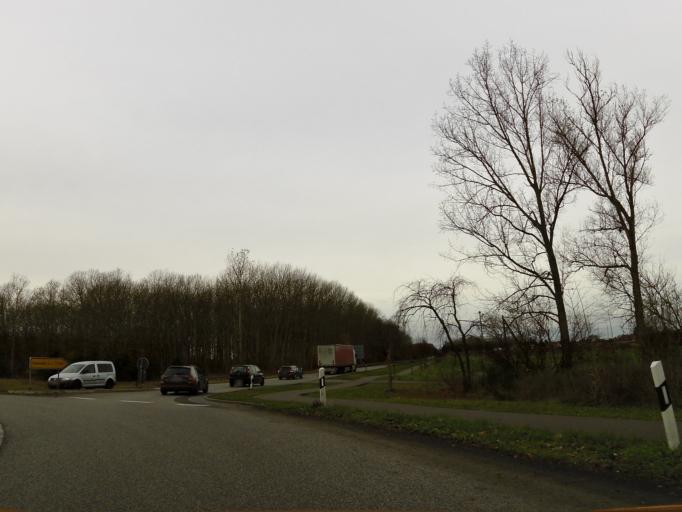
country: DE
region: Saxony-Anhalt
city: Salzwedel
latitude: 52.8322
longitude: 11.1871
